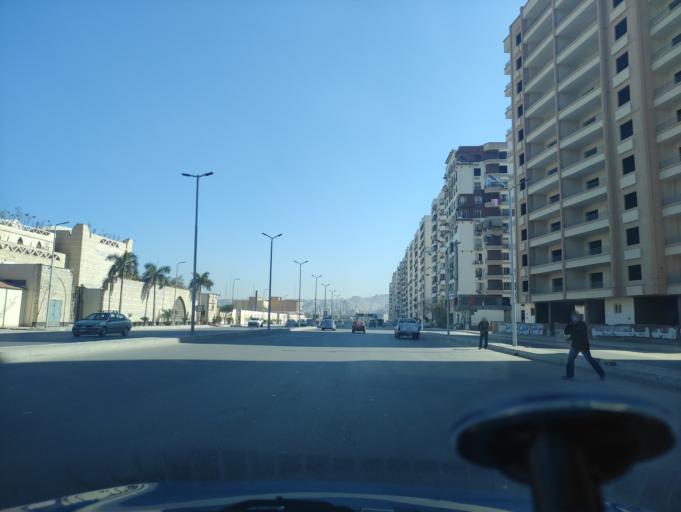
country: EG
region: Al Jizah
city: Al Jizah
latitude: 30.0037
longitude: 31.2440
